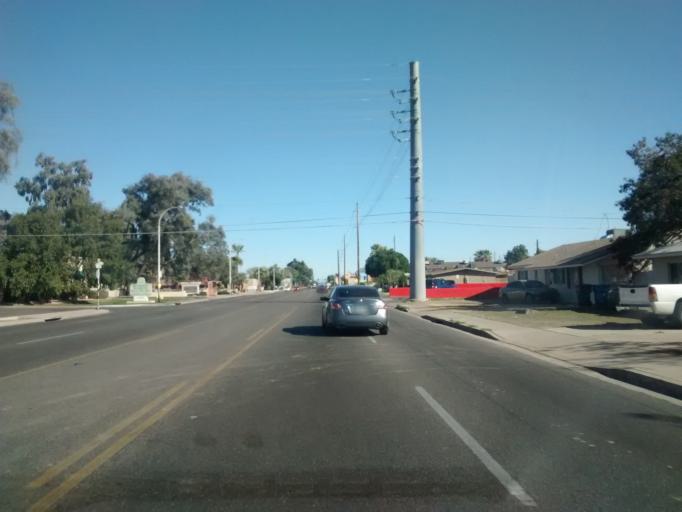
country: US
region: Arizona
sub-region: Maricopa County
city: Glendale
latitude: 33.5239
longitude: -112.1392
